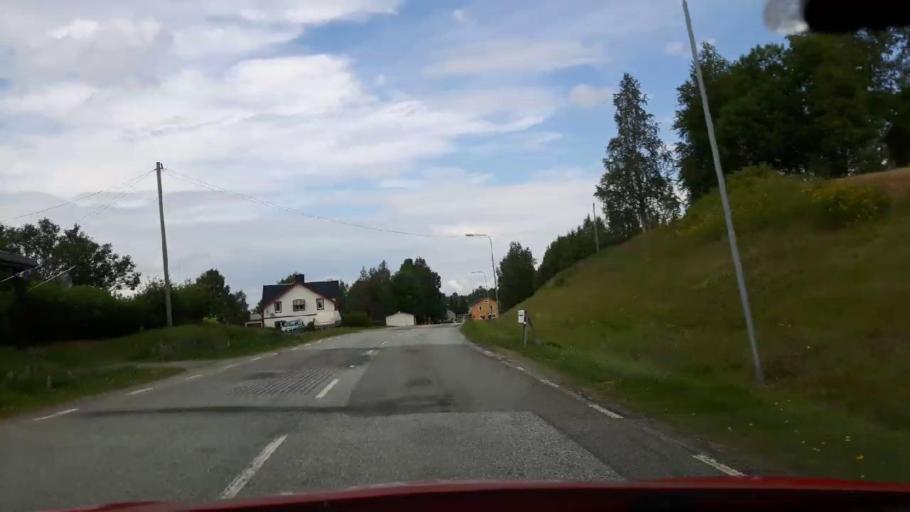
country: SE
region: Jaemtland
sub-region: Stroemsunds Kommun
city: Stroemsund
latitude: 64.4320
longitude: 15.5957
